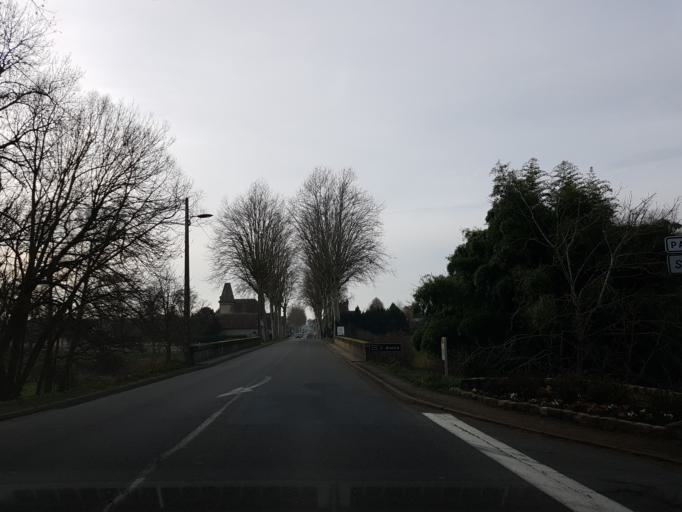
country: FR
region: Auvergne
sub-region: Departement de l'Allier
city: Lusigny
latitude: 46.6117
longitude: 3.5538
